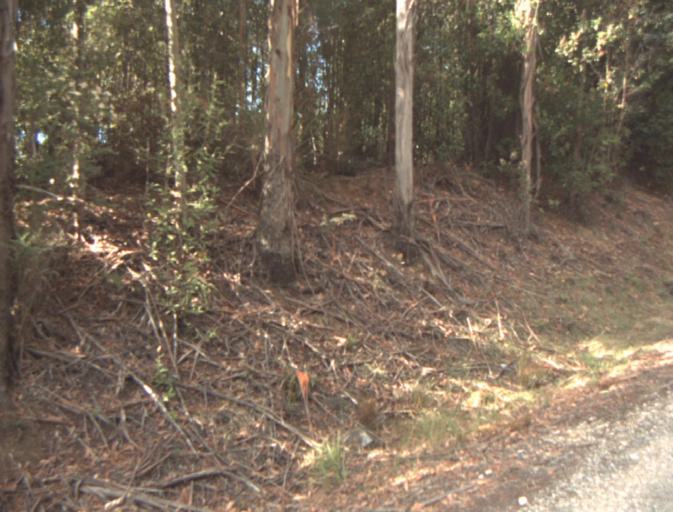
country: AU
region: Tasmania
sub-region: Launceston
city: Mayfield
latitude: -41.2971
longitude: 147.2123
